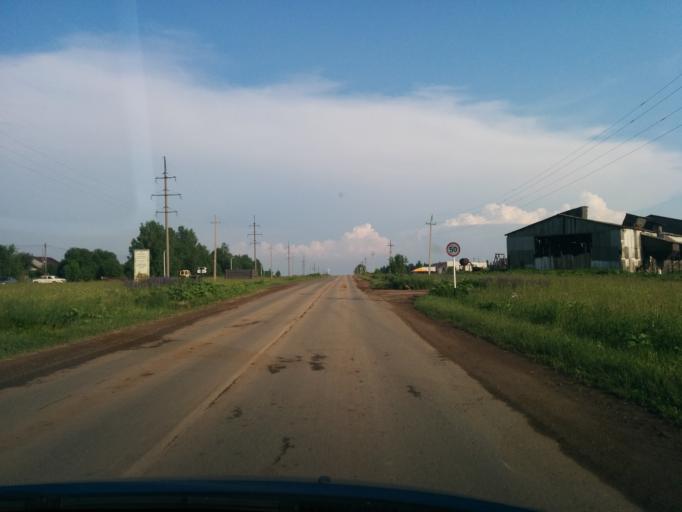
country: RU
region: Perm
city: Polazna
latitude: 58.2294
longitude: 56.2896
